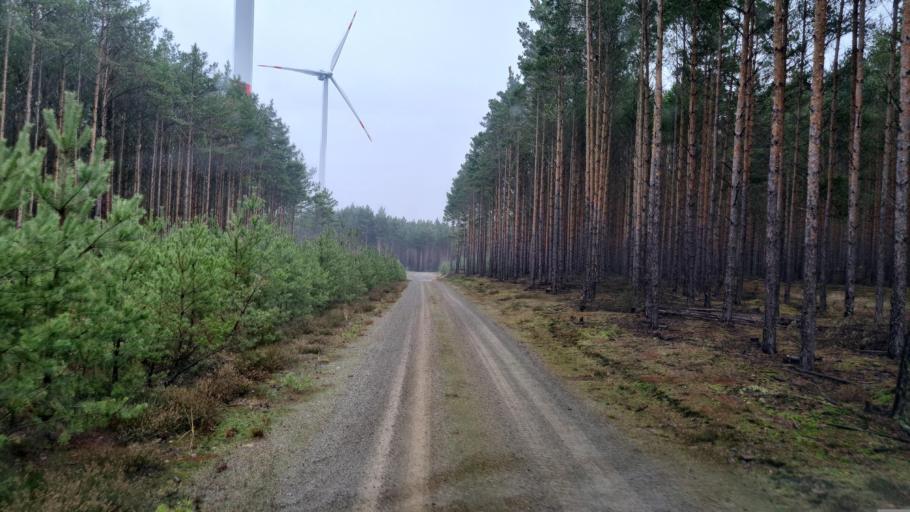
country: DE
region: Brandenburg
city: Sallgast
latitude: 51.6426
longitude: 13.8237
